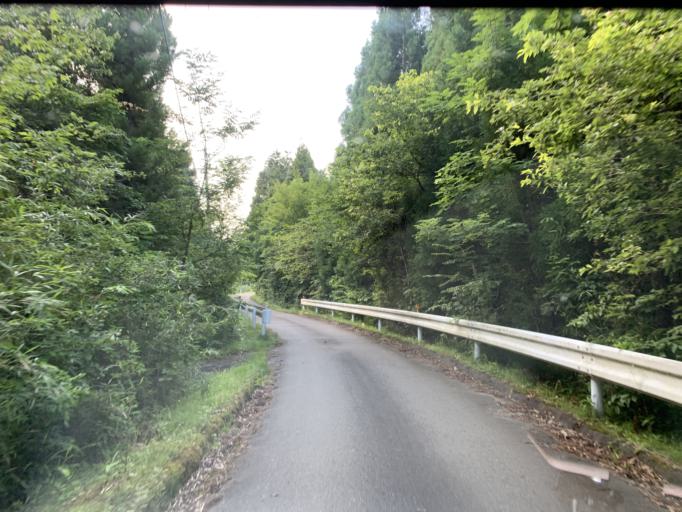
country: JP
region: Iwate
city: Ichinoseki
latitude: 38.8327
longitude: 141.1500
